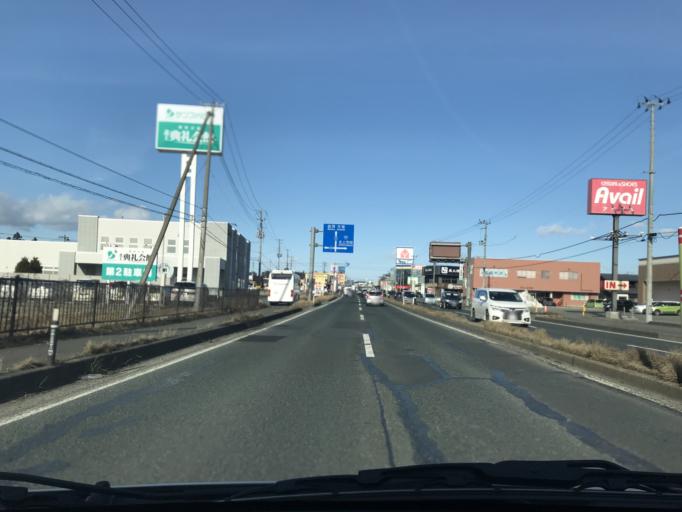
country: JP
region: Iwate
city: Kitakami
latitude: 39.2976
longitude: 141.1067
